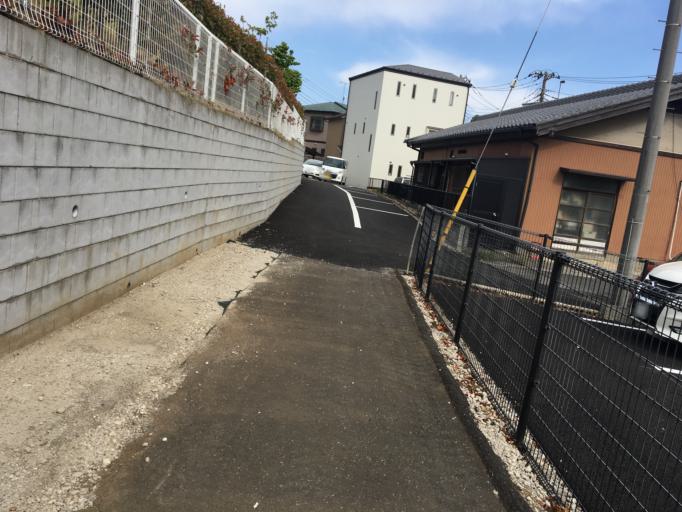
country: JP
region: Saitama
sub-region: Kawaguchi-shi
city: Hatogaya-honcho
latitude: 35.8452
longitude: 139.7388
